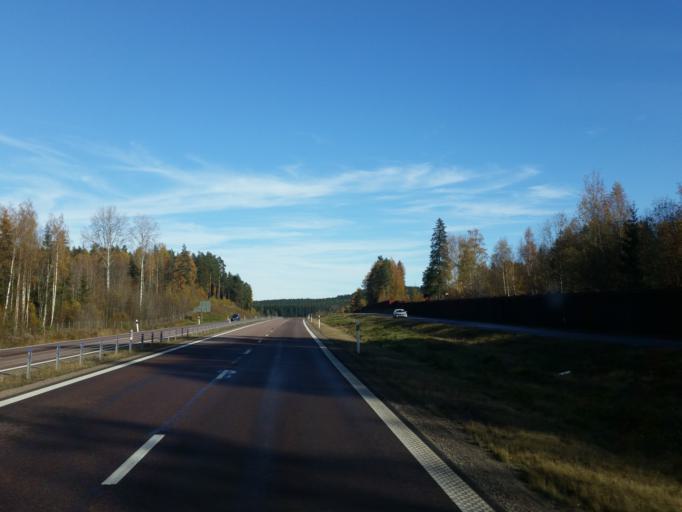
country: SE
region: Dalarna
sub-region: Borlange Kommun
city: Ornas
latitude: 60.5096
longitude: 15.5325
